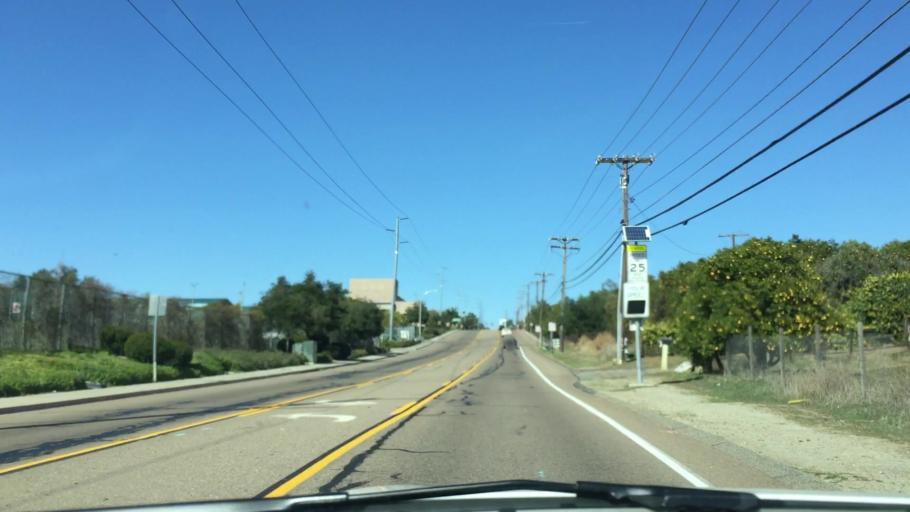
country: US
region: California
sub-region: San Diego County
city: Valley Center
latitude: 33.2771
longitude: -117.0235
